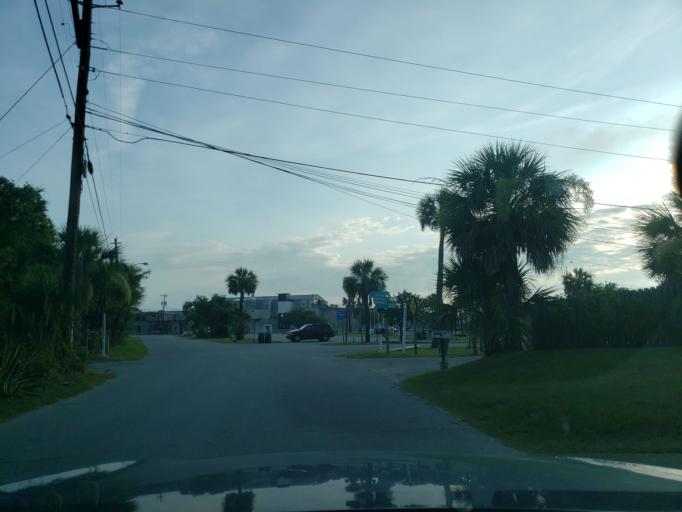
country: US
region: Georgia
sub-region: Chatham County
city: Tybee Island
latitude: 32.0210
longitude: -80.8450
